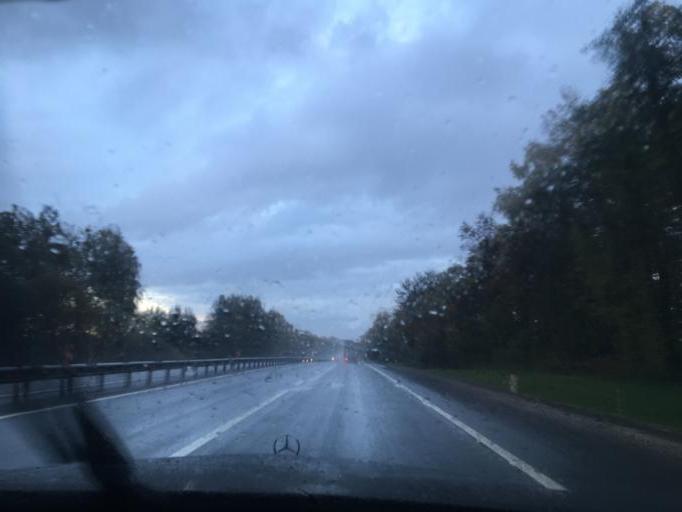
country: RU
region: Smolensk
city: Yartsevo
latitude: 55.0570
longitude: 32.5271
